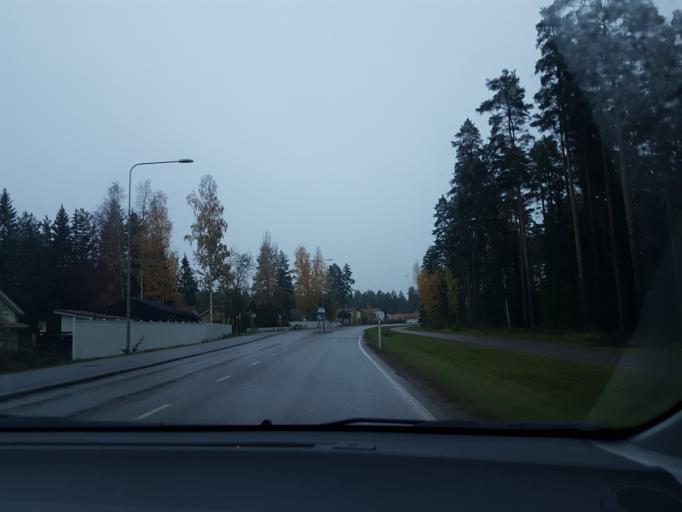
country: FI
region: Uusimaa
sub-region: Helsinki
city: Tuusula
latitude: 60.4002
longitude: 24.9839
